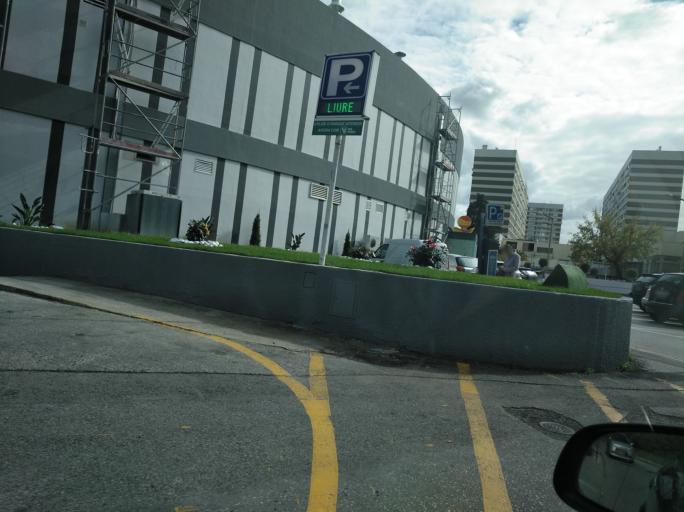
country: PT
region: Lisbon
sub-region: Loures
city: Sacavem
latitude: 38.7828
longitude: -9.1119
